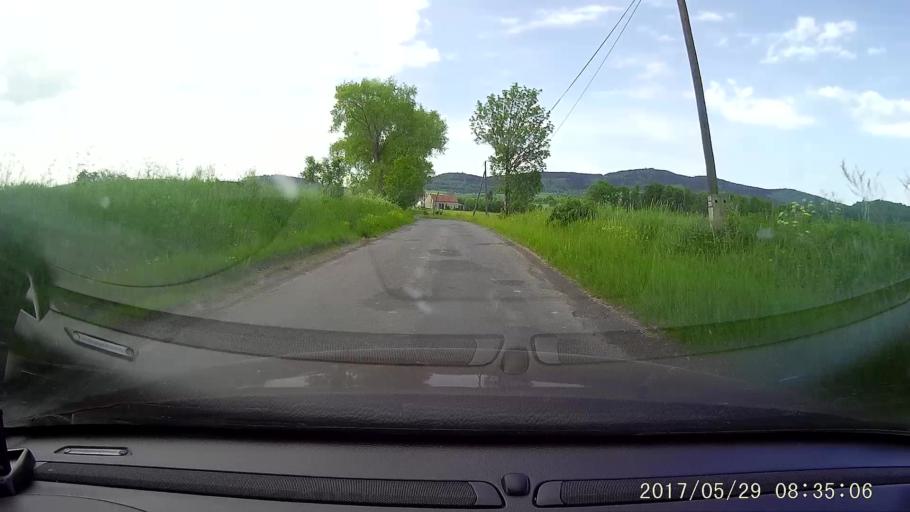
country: PL
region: Lower Silesian Voivodeship
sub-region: Powiat zlotoryjski
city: Swierzawa
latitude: 51.0015
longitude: 15.8613
